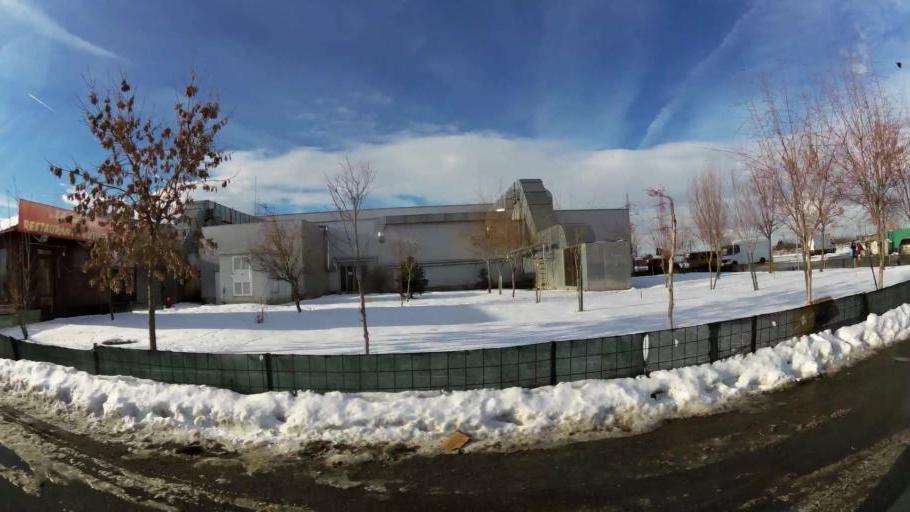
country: RO
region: Ilfov
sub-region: Voluntari City
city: Voluntari
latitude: 44.4772
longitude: 26.1870
